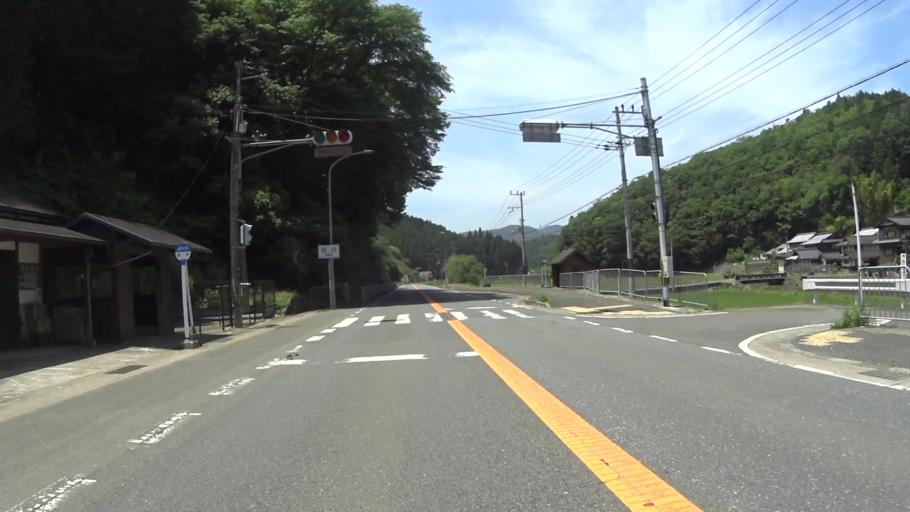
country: JP
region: Kyoto
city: Ayabe
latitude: 35.1843
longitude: 135.3415
